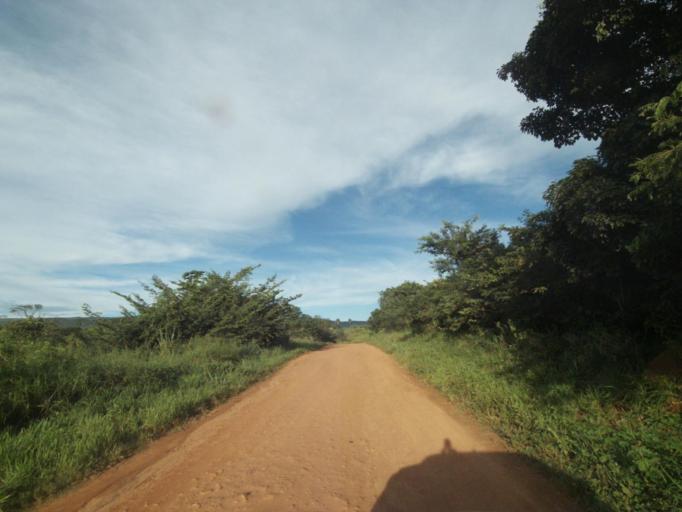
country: BR
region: Goias
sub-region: Jaragua
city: Jaragua
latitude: -15.8431
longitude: -49.3601
